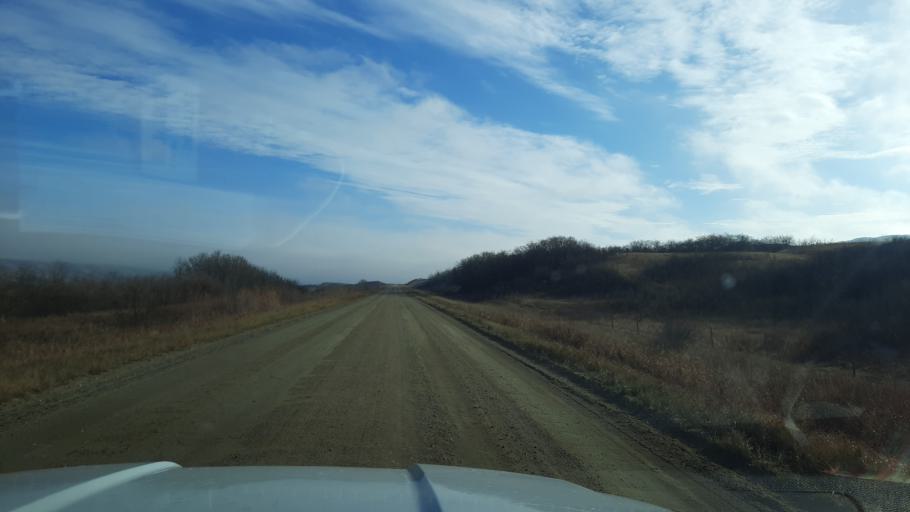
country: CA
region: Saskatchewan
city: Pilot Butte
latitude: 50.7838
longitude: -104.2387
